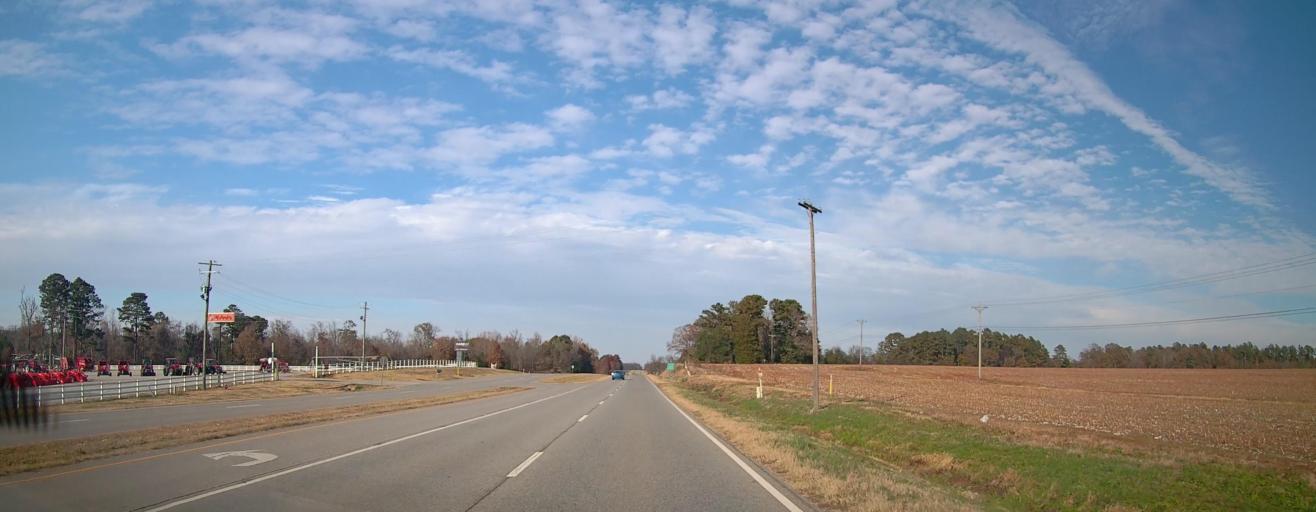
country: US
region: Alabama
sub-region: Morgan County
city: Decatur
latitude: 34.6691
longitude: -86.9499
